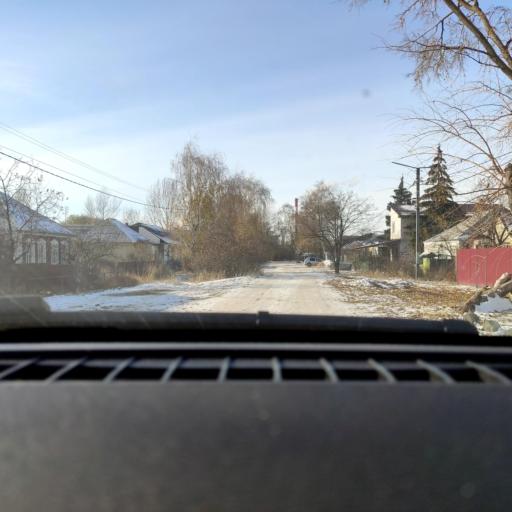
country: RU
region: Voronezj
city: Maslovka
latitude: 51.6311
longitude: 39.2665
